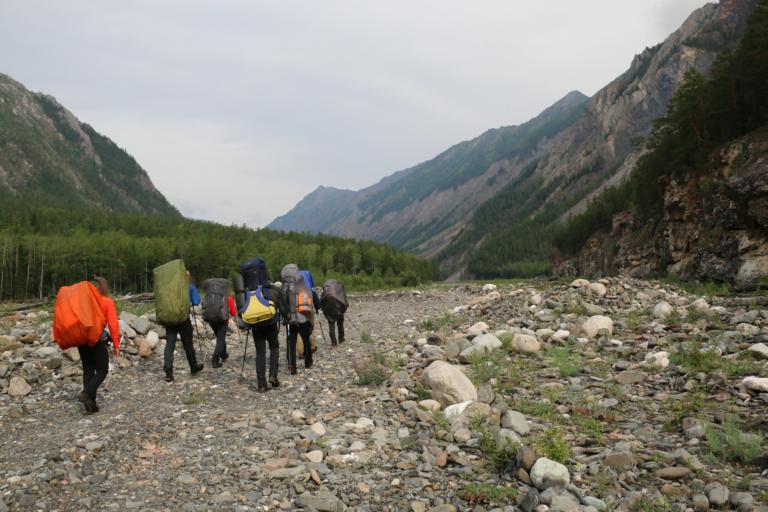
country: RU
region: Respublika Buryatiya
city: Novyy Uoyan
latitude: 56.2559
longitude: 111.4788
